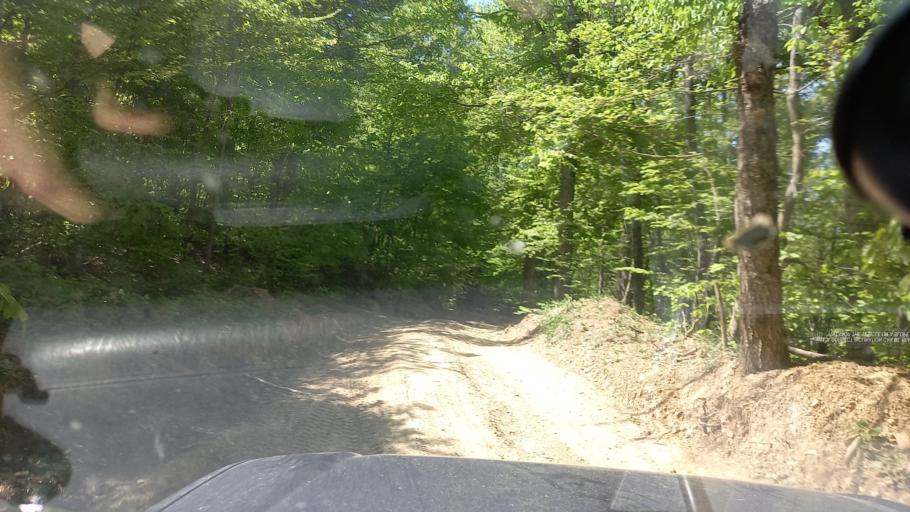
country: RU
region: Krasnodarskiy
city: Shepsi
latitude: 44.2479
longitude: 39.2983
